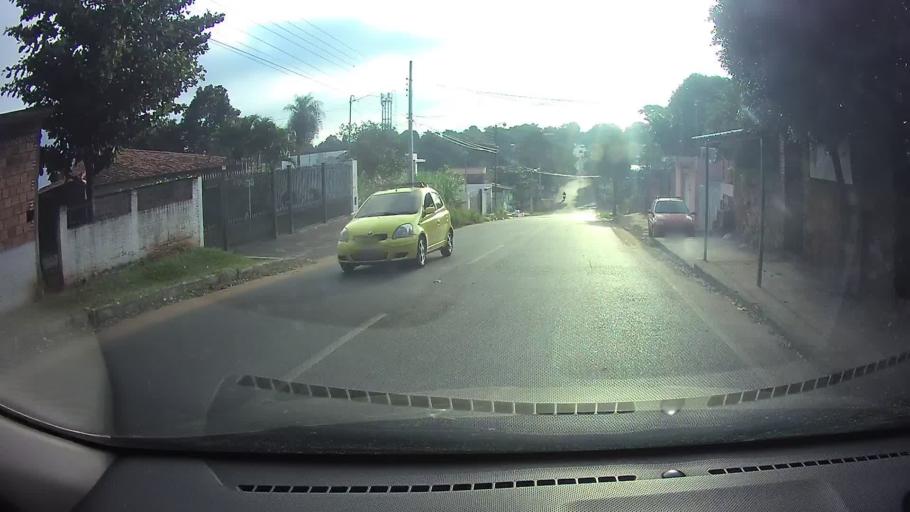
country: PY
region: Central
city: Fernando de la Mora
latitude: -25.3450
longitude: -57.5558
